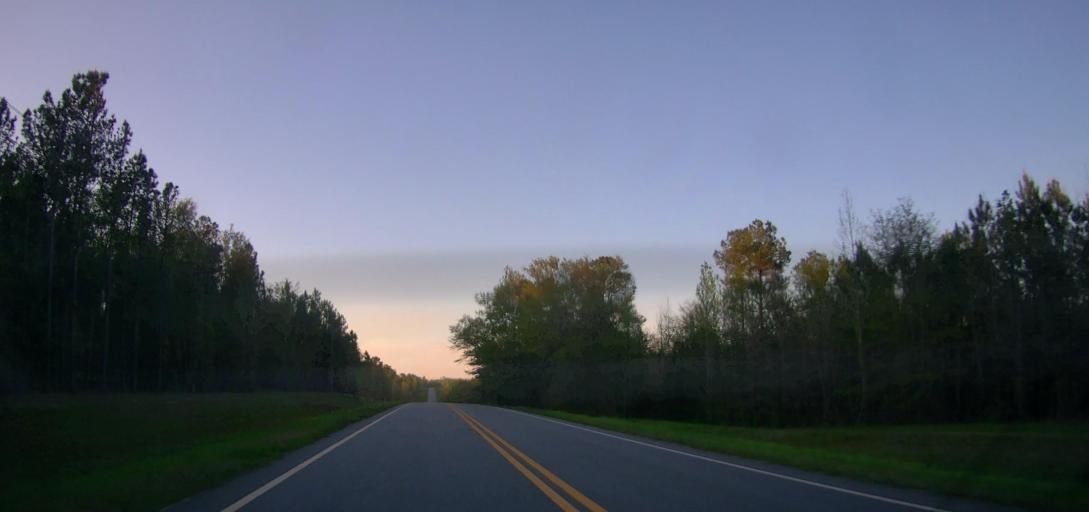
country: US
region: Georgia
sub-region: Talbot County
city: Talbotton
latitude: 32.5456
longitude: -84.5698
